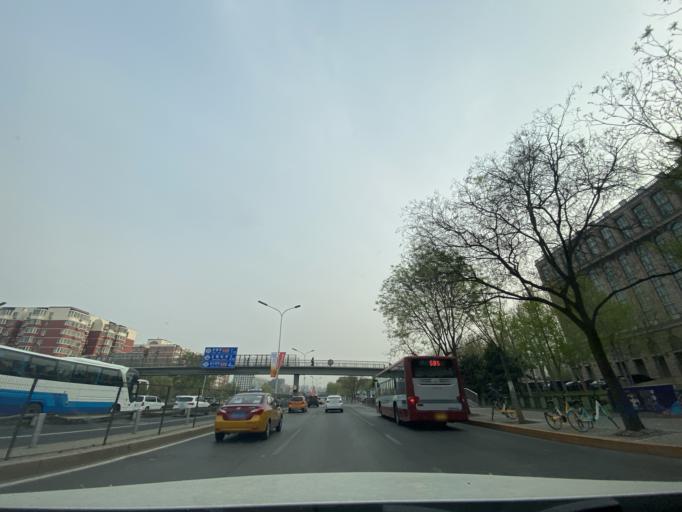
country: CN
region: Beijing
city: Sijiqing
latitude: 39.9358
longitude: 116.2680
